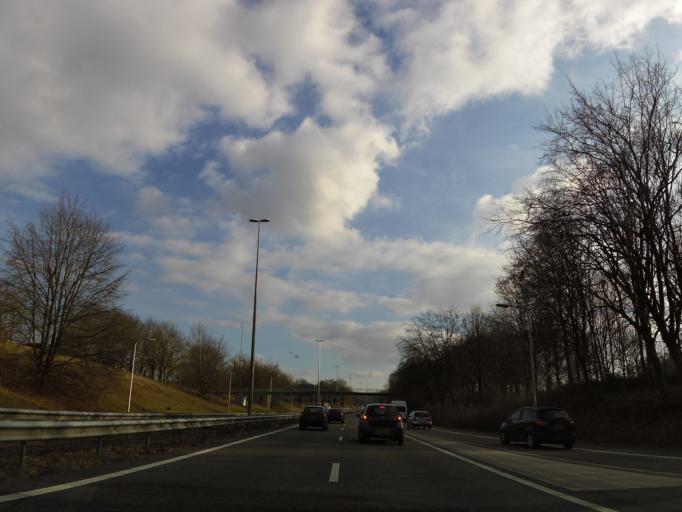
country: NL
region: Limburg
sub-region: Gemeente Heerlen
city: Heerlen
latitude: 50.8780
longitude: 5.9739
